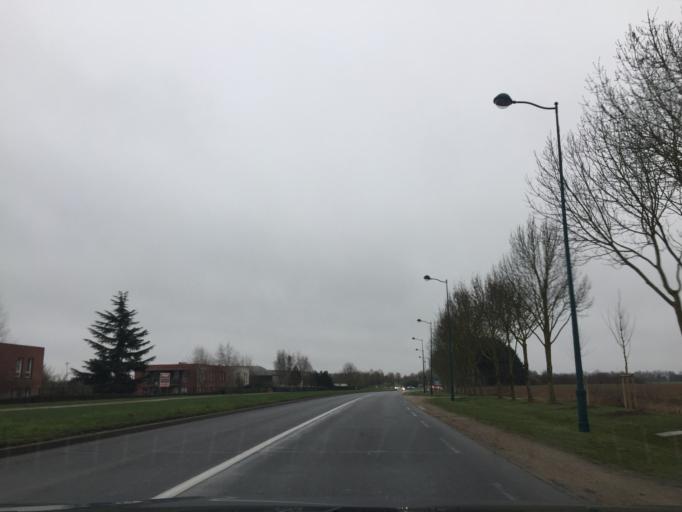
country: FR
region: Ile-de-France
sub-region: Departement de Seine-et-Marne
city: Magny-le-Hongre
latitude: 48.8649
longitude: 2.8077
